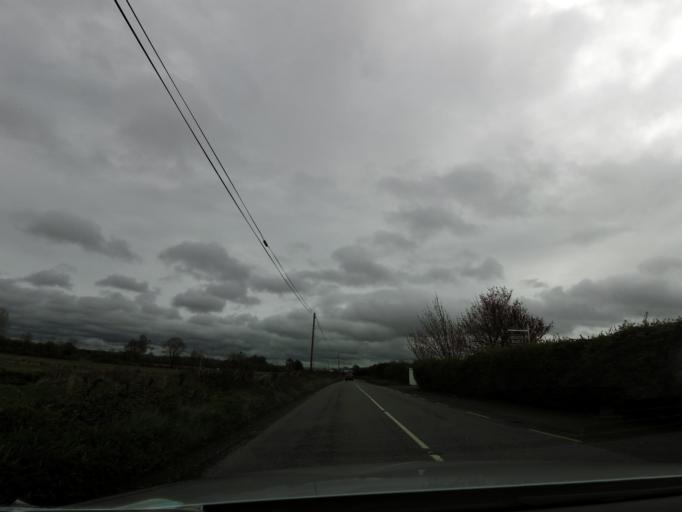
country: IE
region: Leinster
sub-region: Kilkenny
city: Ballyragget
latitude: 52.7303
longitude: -7.3866
